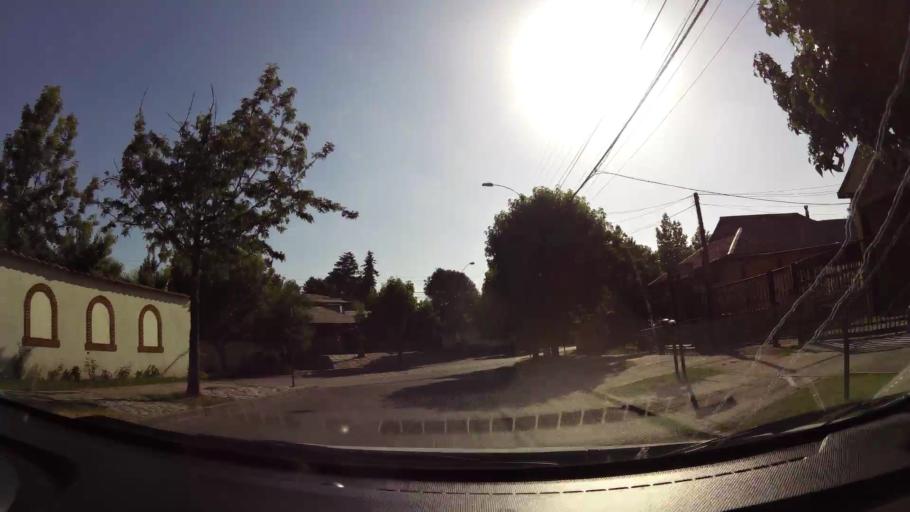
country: CL
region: Maule
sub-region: Provincia de Talca
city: Talca
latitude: -35.4154
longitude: -71.6696
